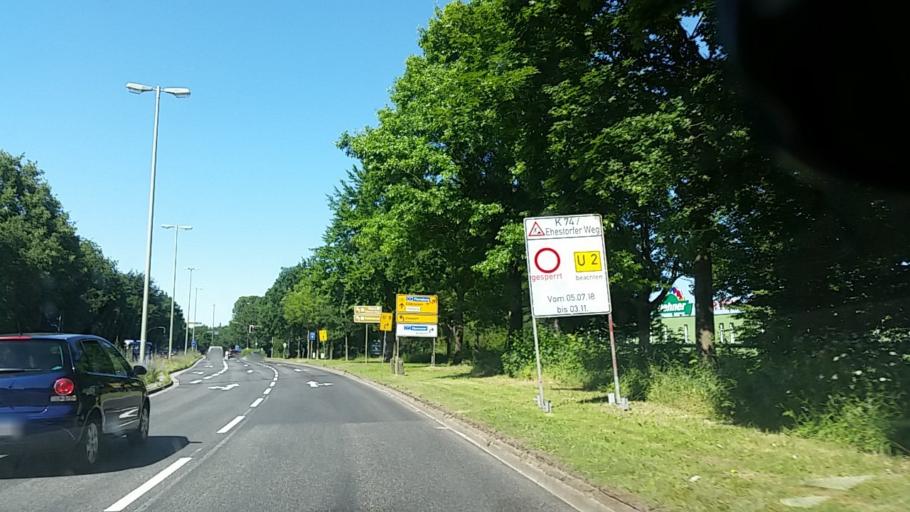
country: DE
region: Lower Saxony
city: Seevetal
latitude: 53.4296
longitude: 9.9319
